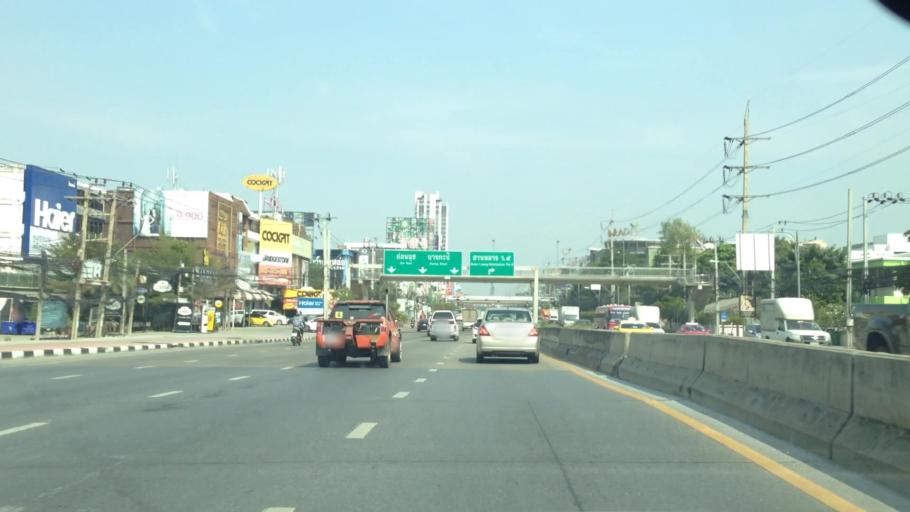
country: TH
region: Bangkok
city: Bang Na
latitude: 13.6835
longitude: 100.6465
